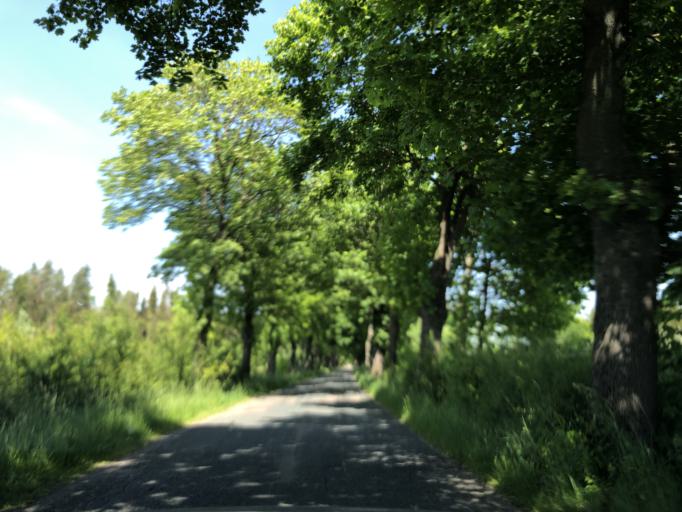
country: PL
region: West Pomeranian Voivodeship
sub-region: Powiat kolobrzeski
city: Goscino
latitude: 54.0200
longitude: 15.7368
